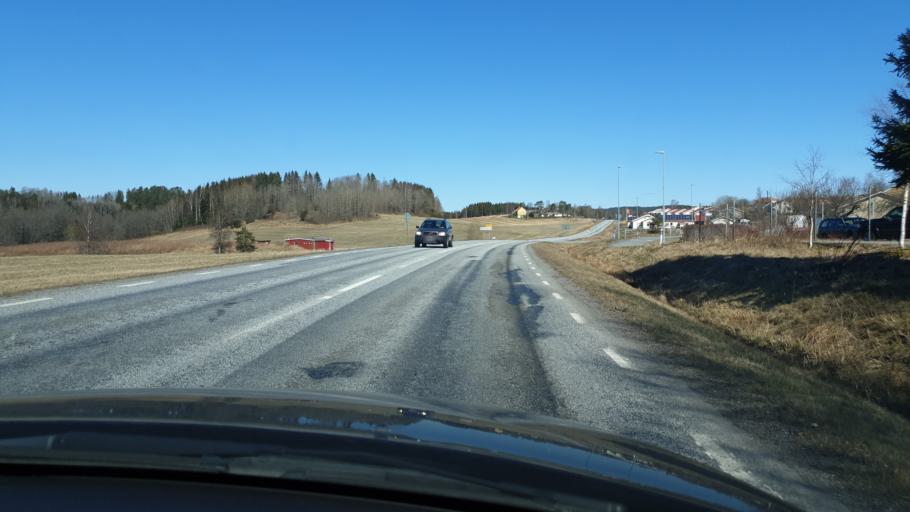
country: SE
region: Vaestra Goetaland
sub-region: Tanums Kommun
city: Tanumshede
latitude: 58.7700
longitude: 11.5566
